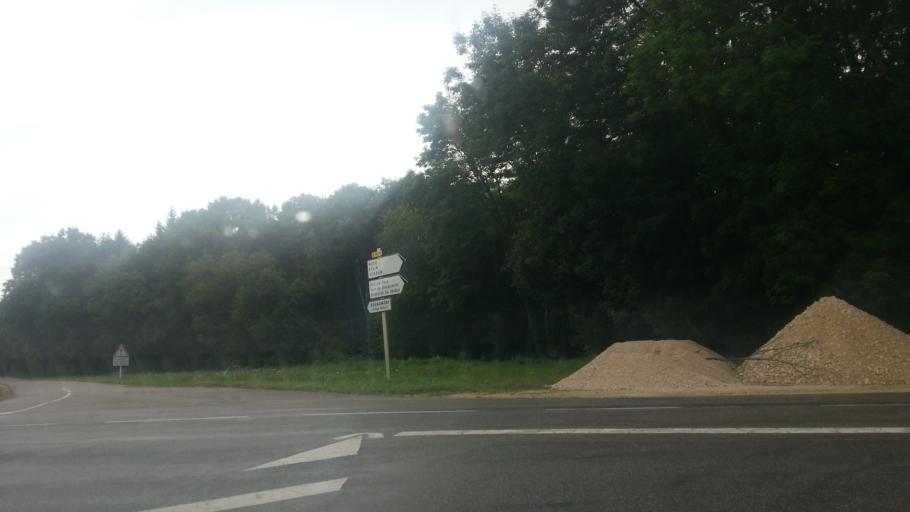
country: FR
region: Lorraine
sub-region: Departement de la Meuse
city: Verdun
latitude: 49.2097
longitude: 5.4276
